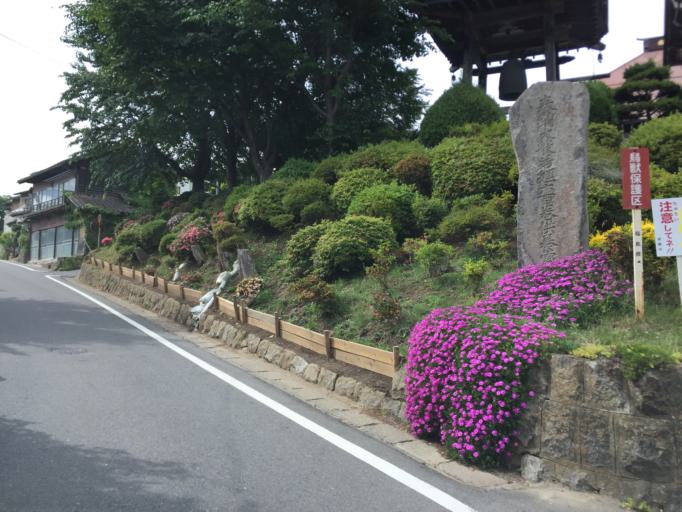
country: JP
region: Fukushima
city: Funehikimachi-funehiki
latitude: 37.4392
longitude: 140.6420
